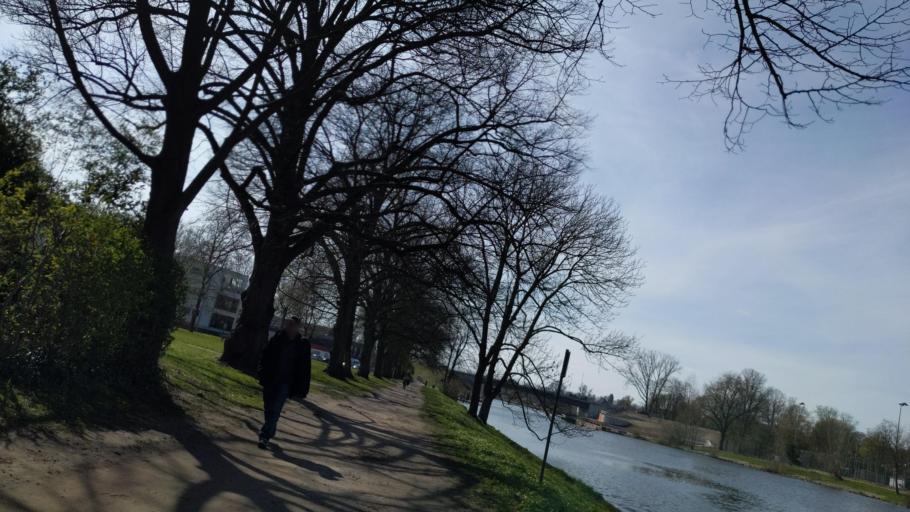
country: DE
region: Schleswig-Holstein
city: Luebeck
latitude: 53.8562
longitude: 10.6849
